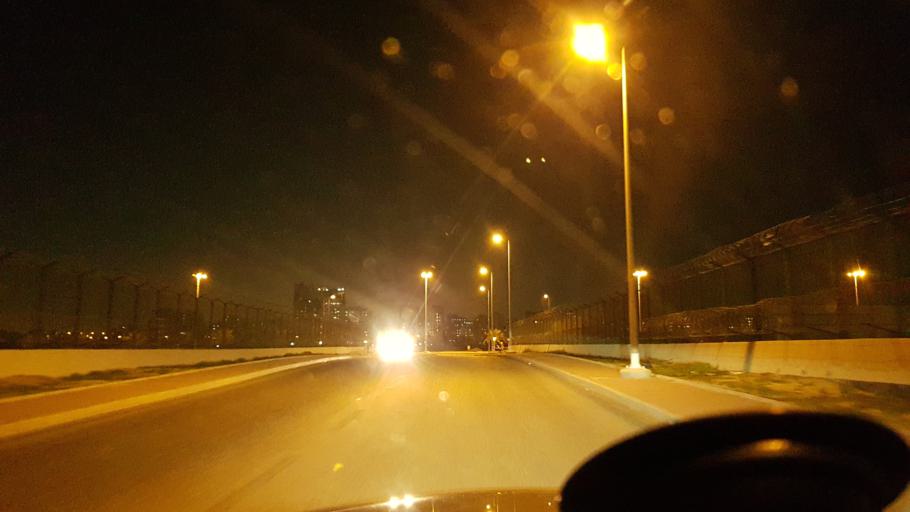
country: KW
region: Al Ahmadi
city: Al Manqaf
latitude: 29.1189
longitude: 48.1288
